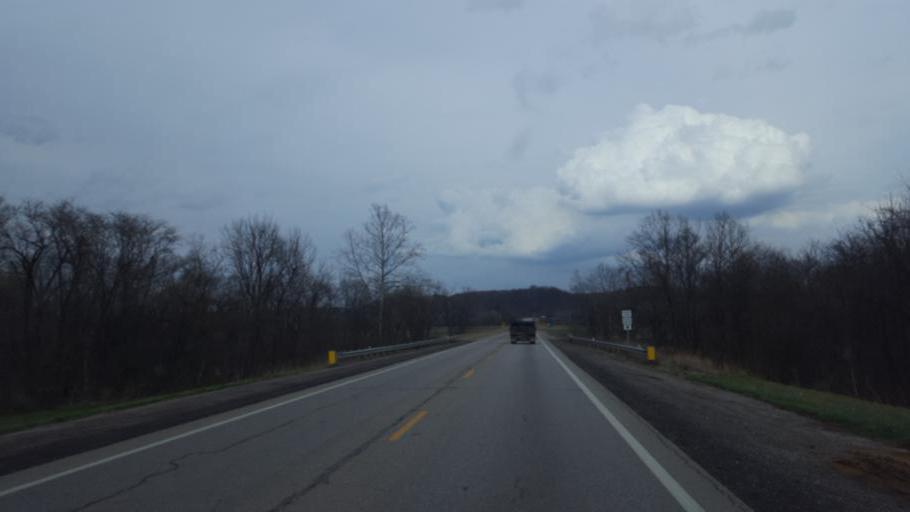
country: US
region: Ohio
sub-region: Coshocton County
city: Coshocton
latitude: 40.2359
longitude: -81.8736
